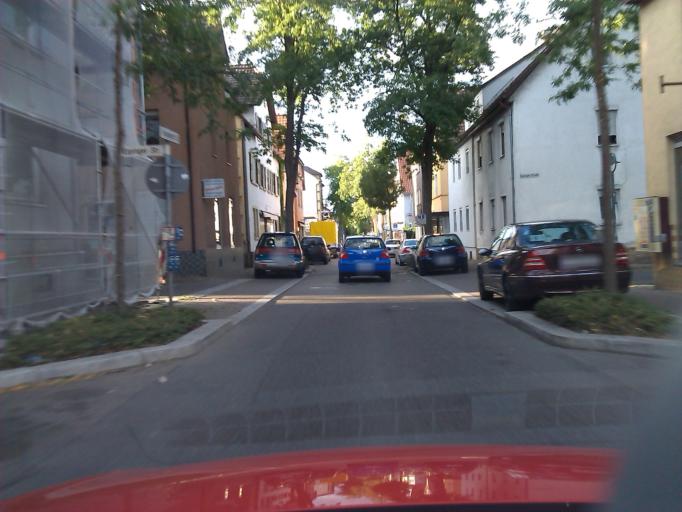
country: DE
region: Baden-Wuerttemberg
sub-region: Regierungsbezirk Stuttgart
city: Heilbronn
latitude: 49.1357
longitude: 9.1920
